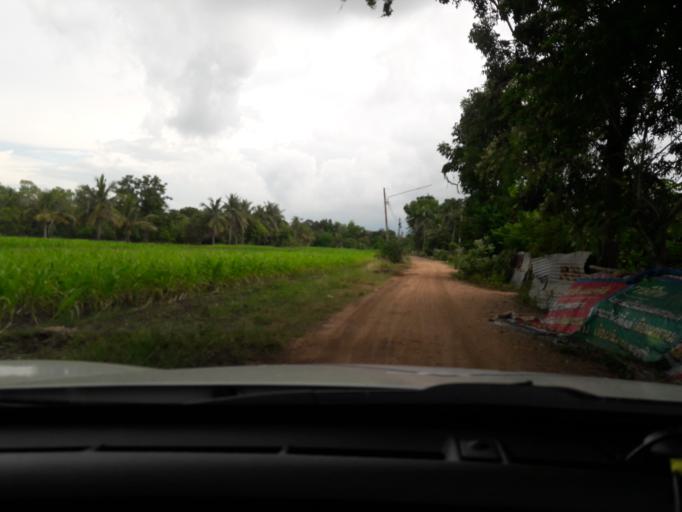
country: TH
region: Nakhon Sawan
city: Tak Fa
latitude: 15.3582
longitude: 100.4948
